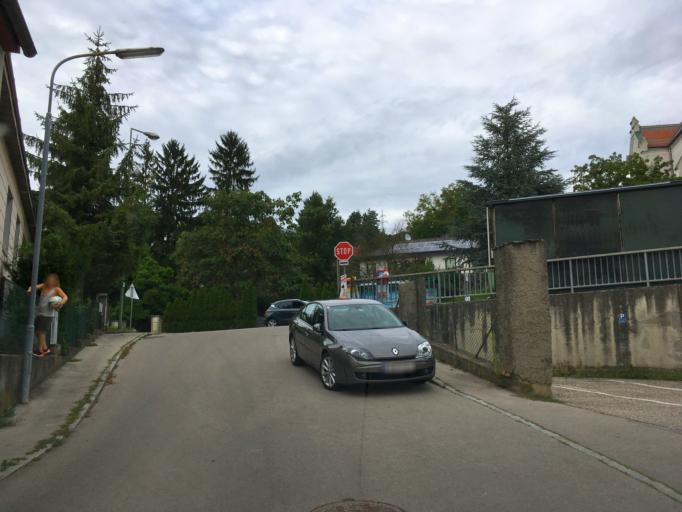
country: AT
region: Lower Austria
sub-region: Politischer Bezirk Tulln
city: Wordern
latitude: 48.3123
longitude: 16.2503
